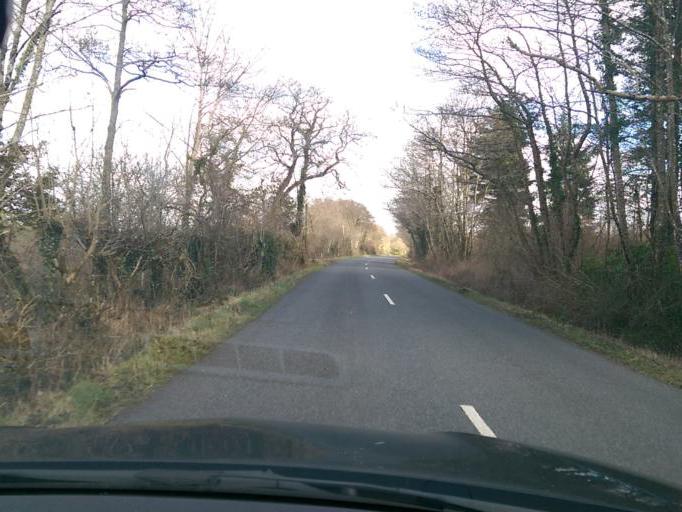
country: IE
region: Connaught
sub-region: County Galway
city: Loughrea
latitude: 53.4670
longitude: -8.5305
